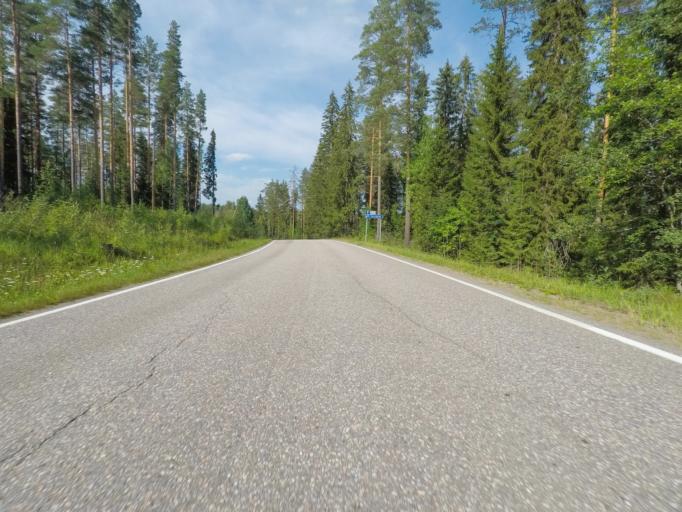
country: FI
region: Southern Savonia
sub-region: Savonlinna
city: Sulkava
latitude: 61.7803
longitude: 28.2393
